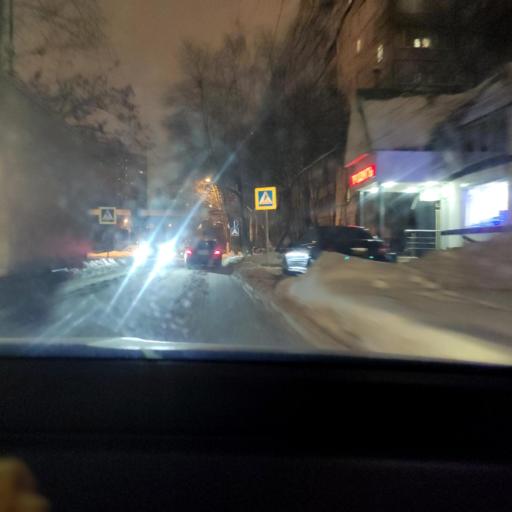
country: RU
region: Moskovskaya
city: Odintsovo
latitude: 55.6772
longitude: 37.2874
